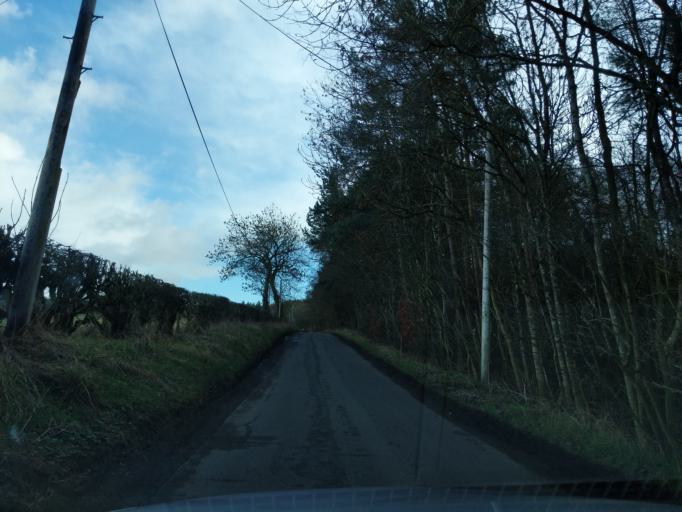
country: GB
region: Scotland
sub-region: Edinburgh
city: Balerno
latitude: 55.8755
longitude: -3.3208
